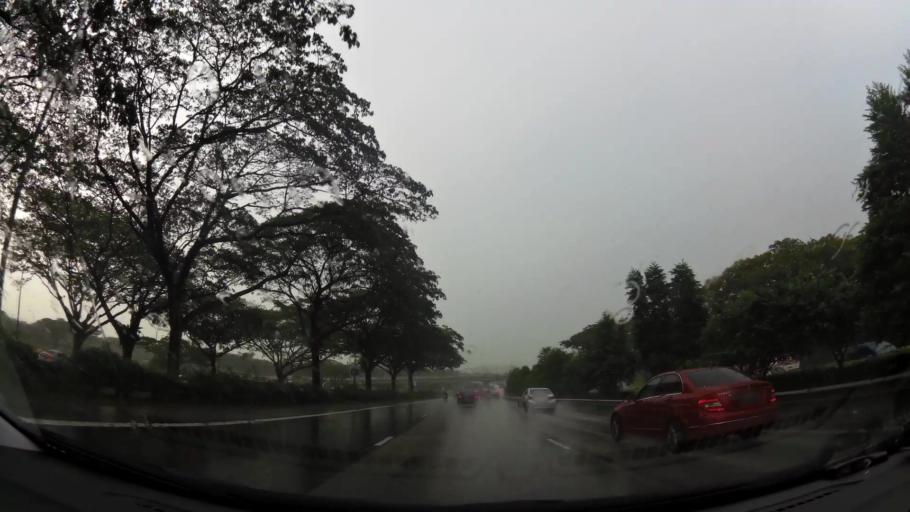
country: MY
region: Johor
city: Kampung Pasir Gudang Baru
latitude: 1.3806
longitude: 103.9193
